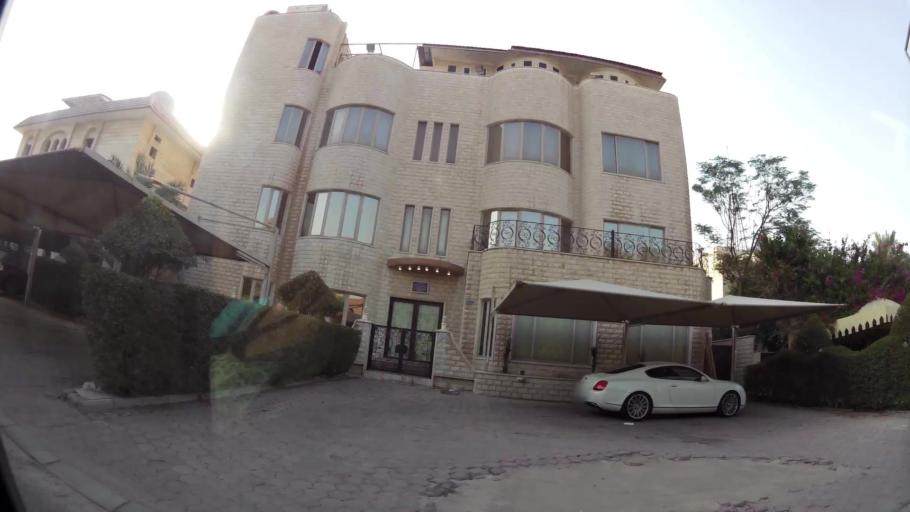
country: KW
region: Muhafazat Hawalli
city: Ar Rumaythiyah
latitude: 29.3208
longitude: 48.0770
